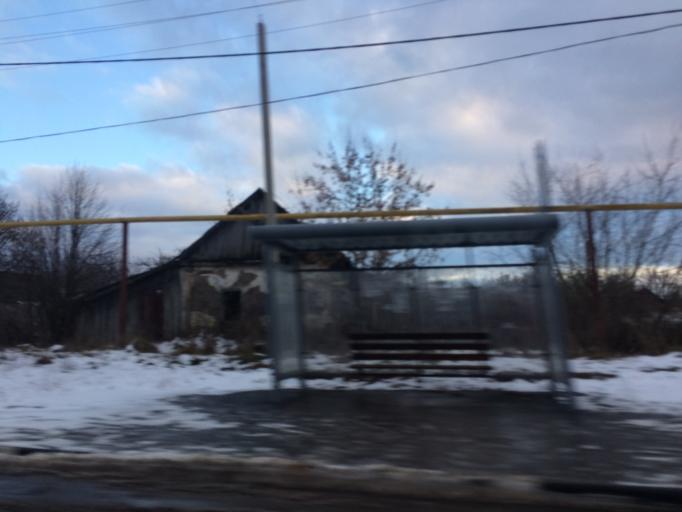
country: RU
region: Tula
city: Cherepet'
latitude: 54.1196
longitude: 36.3664
